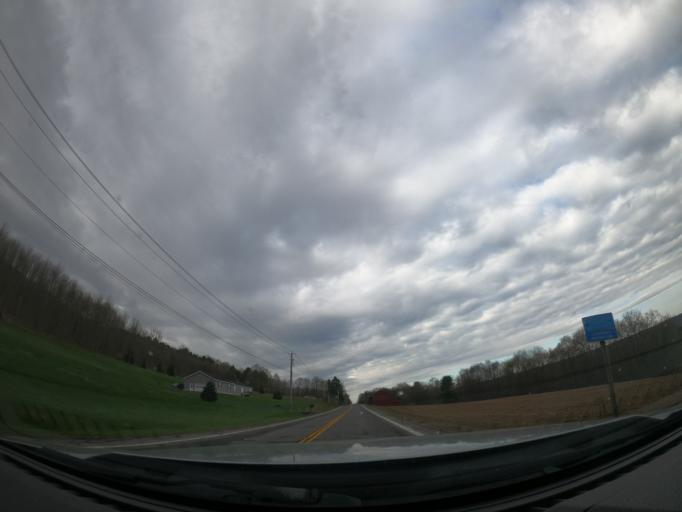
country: US
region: New York
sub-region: Madison County
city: Cazenovia
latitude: 42.7955
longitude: -75.8601
